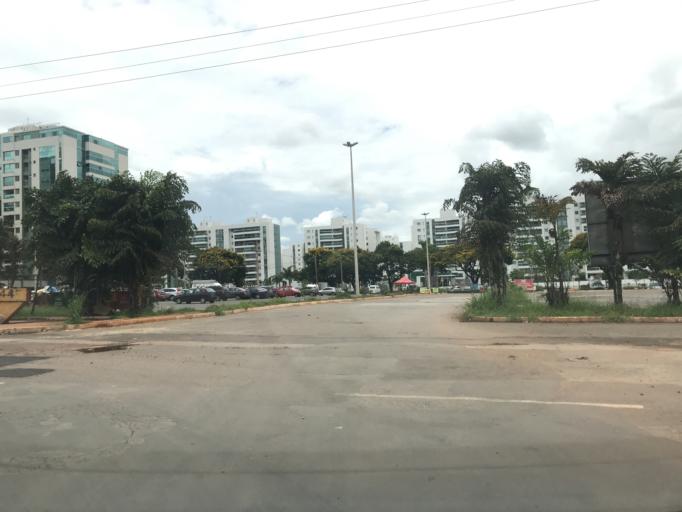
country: BR
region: Federal District
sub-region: Brasilia
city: Brasilia
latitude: -15.8273
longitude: -47.9575
